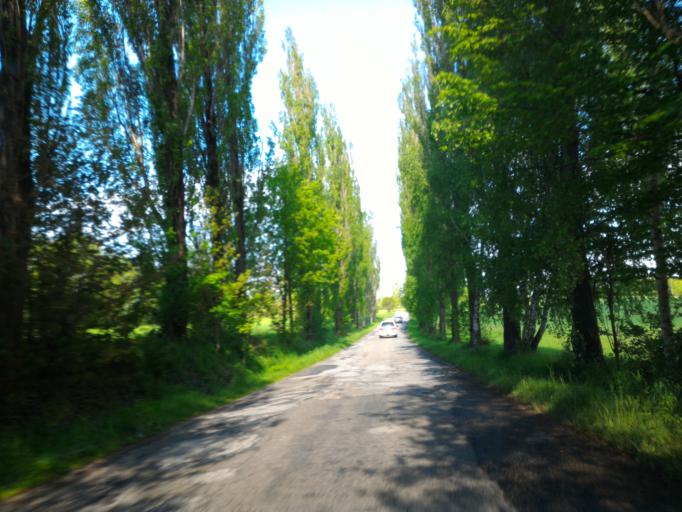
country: CZ
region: Vysocina
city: Ledec nad Sazavou
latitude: 49.6521
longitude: 15.2864
